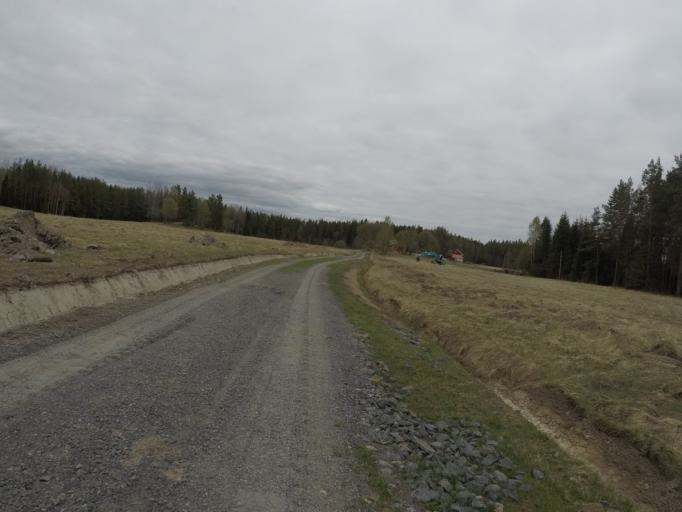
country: SE
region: Soedermanland
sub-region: Eskilstuna Kommun
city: Kvicksund
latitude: 59.4007
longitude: 16.3054
